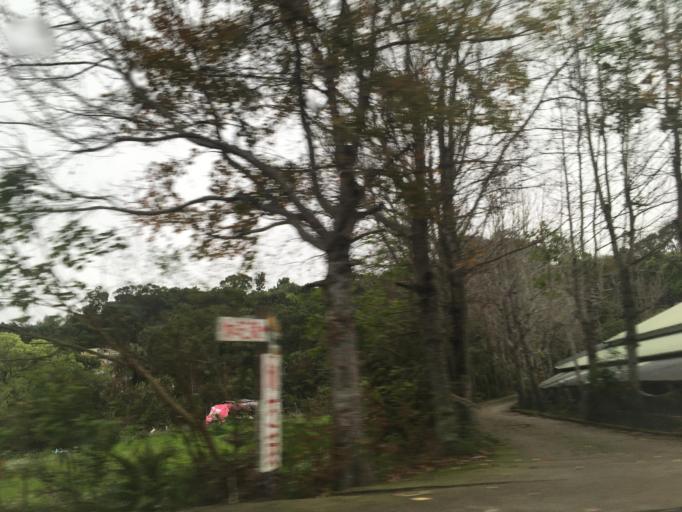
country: TW
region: Taiwan
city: Fengyuan
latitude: 24.4198
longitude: 120.7305
